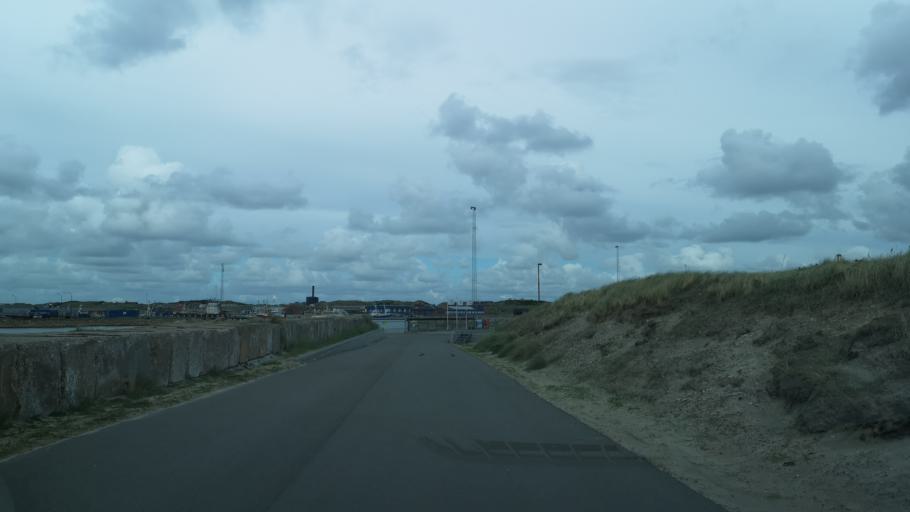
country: DK
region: Central Jutland
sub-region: Ringkobing-Skjern Kommune
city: Hvide Sande
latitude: 56.0000
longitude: 8.1216
